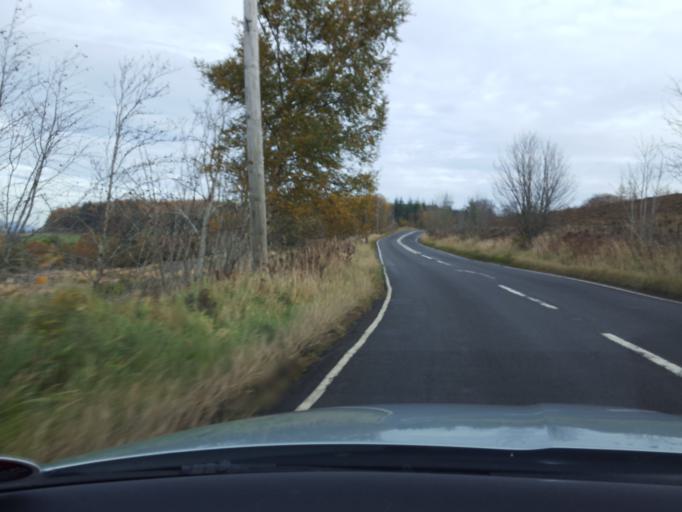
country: GB
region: Scotland
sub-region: The Scottish Borders
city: West Linton
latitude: 55.6845
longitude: -3.4365
